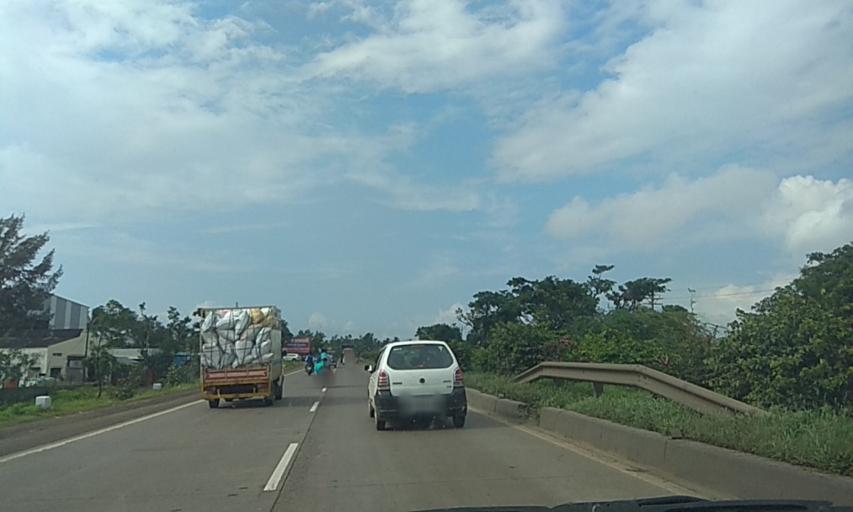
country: IN
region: Maharashtra
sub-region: Kolhapur
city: Kodoli
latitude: 16.8046
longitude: 74.2850
